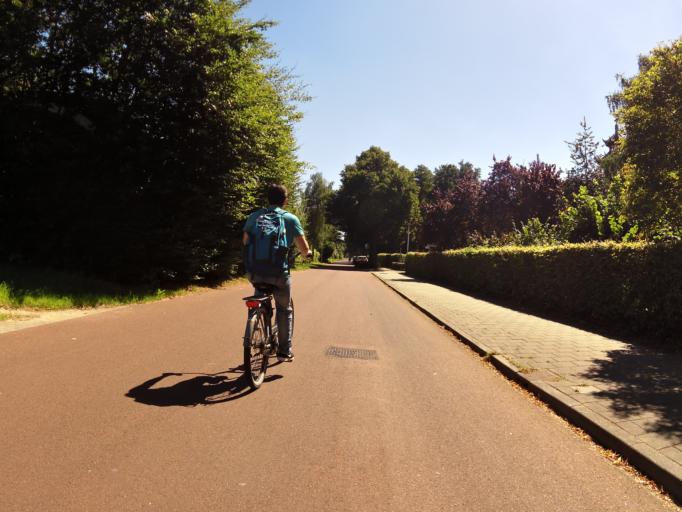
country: NL
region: Gelderland
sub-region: Gemeente Nijmegen
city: Nijmegen
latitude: 51.8298
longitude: 5.8623
